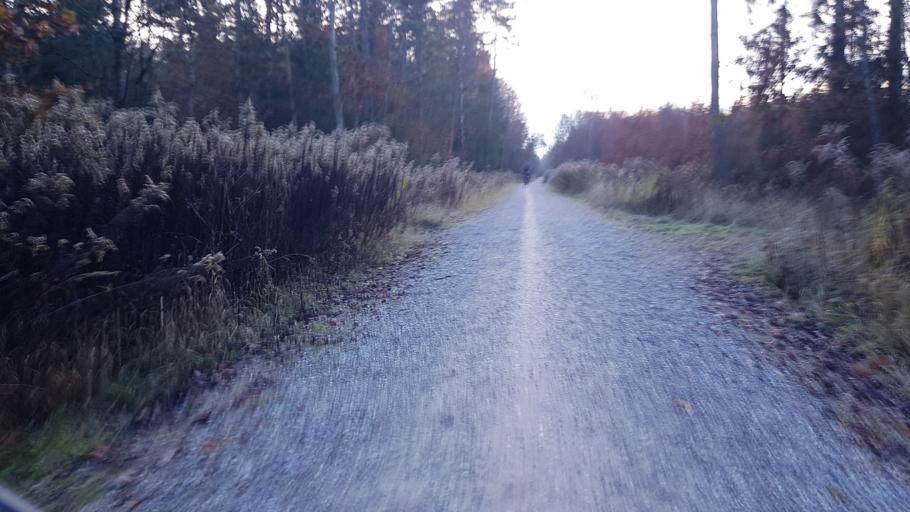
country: DE
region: Bavaria
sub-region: Upper Bavaria
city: Unterhaching
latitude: 48.0788
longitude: 11.5921
